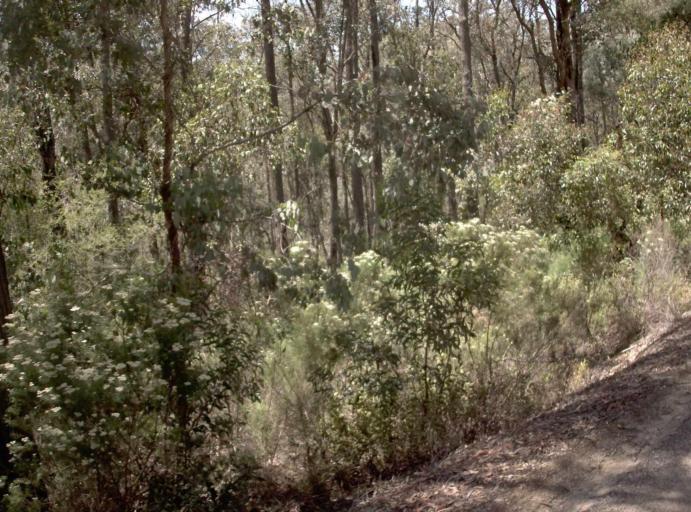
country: AU
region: Victoria
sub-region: East Gippsland
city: Lakes Entrance
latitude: -37.6246
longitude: 147.8835
